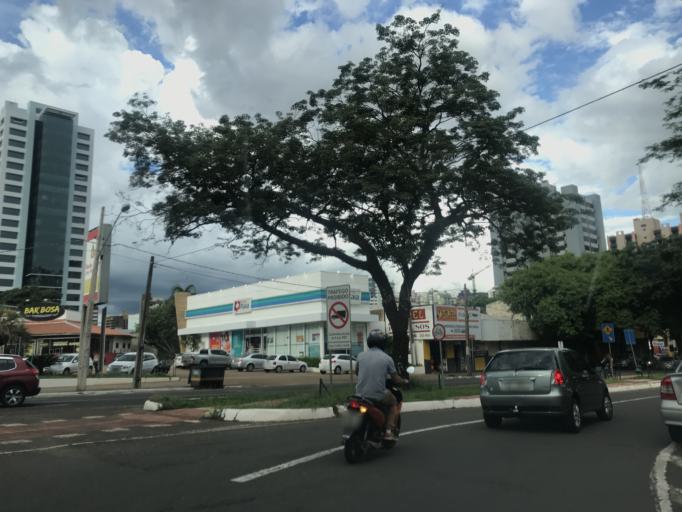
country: BR
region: Parana
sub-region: Maringa
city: Maringa
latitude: -23.4209
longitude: -51.9465
